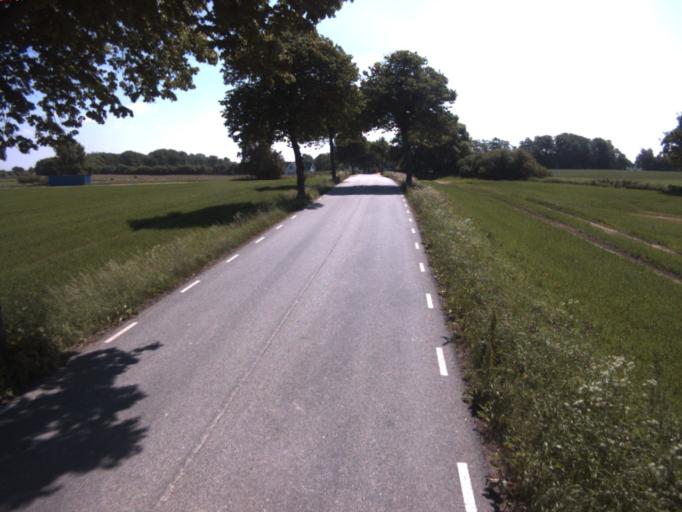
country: SE
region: Skane
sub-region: Helsingborg
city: Odakra
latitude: 56.1110
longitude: 12.6799
